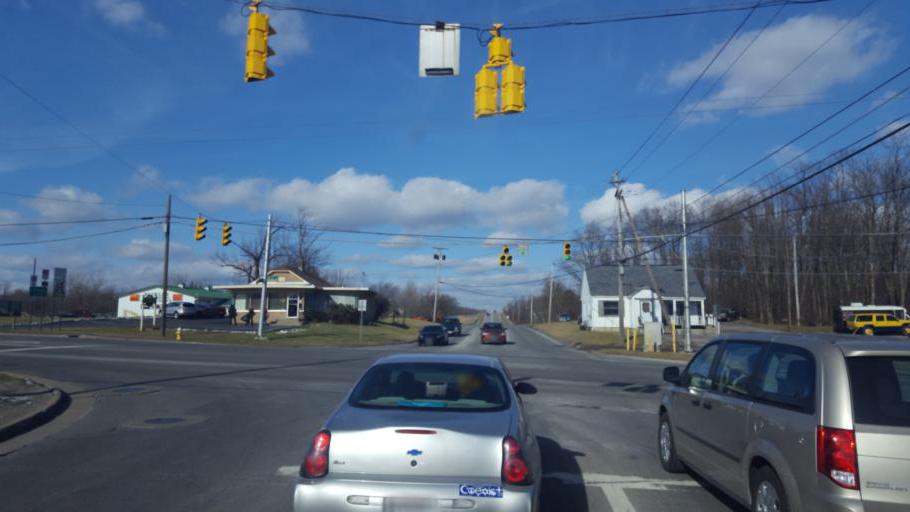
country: US
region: Ohio
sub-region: Richland County
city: Ontario
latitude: 40.7689
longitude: -82.5708
